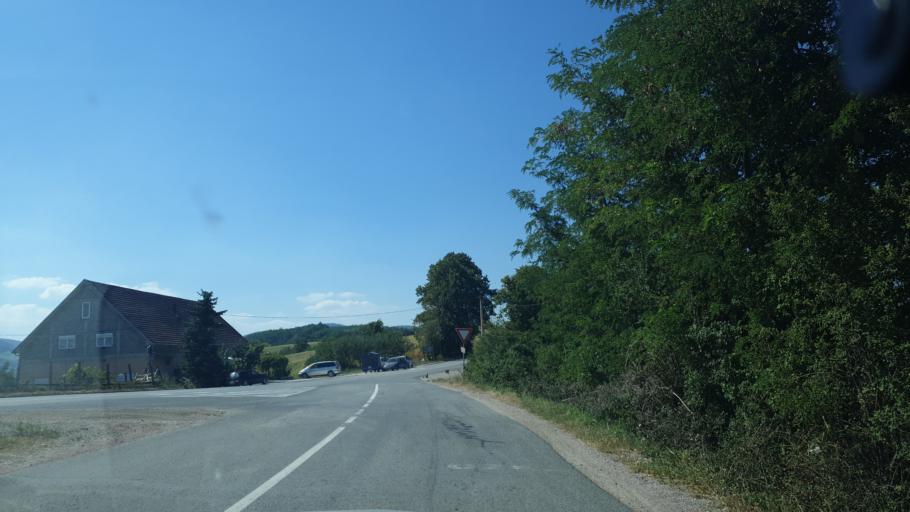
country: RS
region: Central Serbia
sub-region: Kolubarski Okrug
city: Mionica
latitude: 44.1759
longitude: 20.0346
